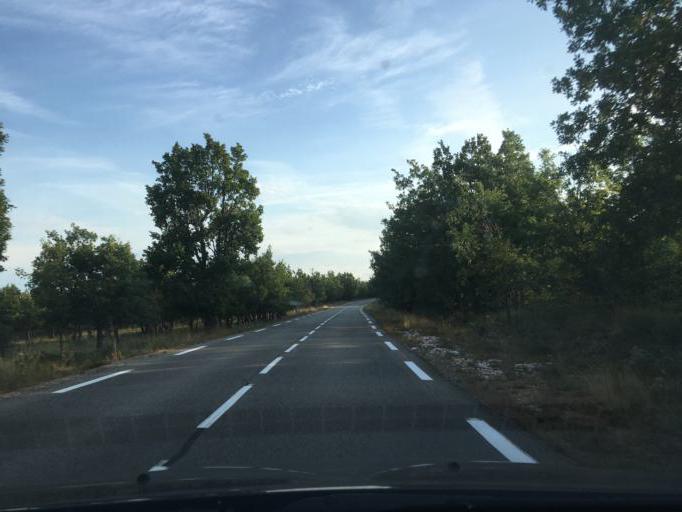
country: FR
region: Provence-Alpes-Cote d'Azur
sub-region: Departement du Var
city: Aups
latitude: 43.7117
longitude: 6.2194
